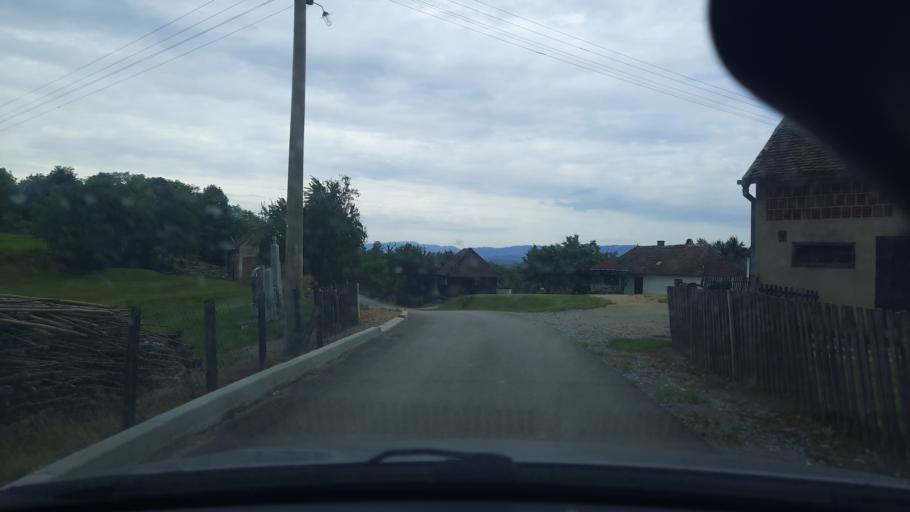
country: RS
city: Jarebice
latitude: 44.4990
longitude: 19.4760
